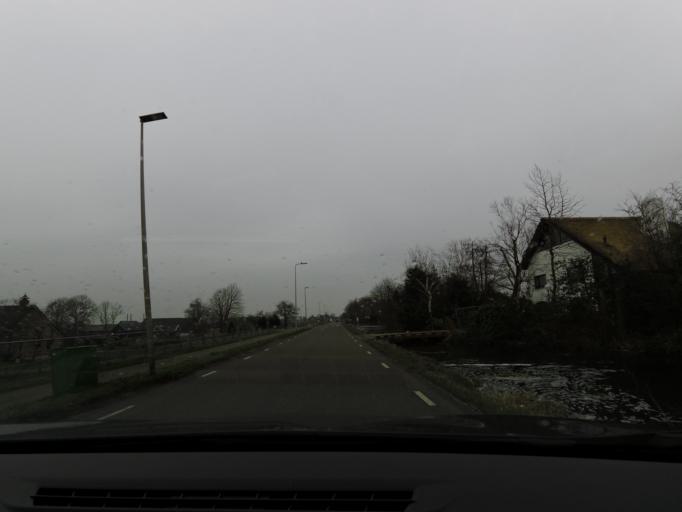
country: NL
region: South Holland
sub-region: Gemeente Nieuwkoop
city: Nieuwkoop
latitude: 52.1588
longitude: 4.8018
